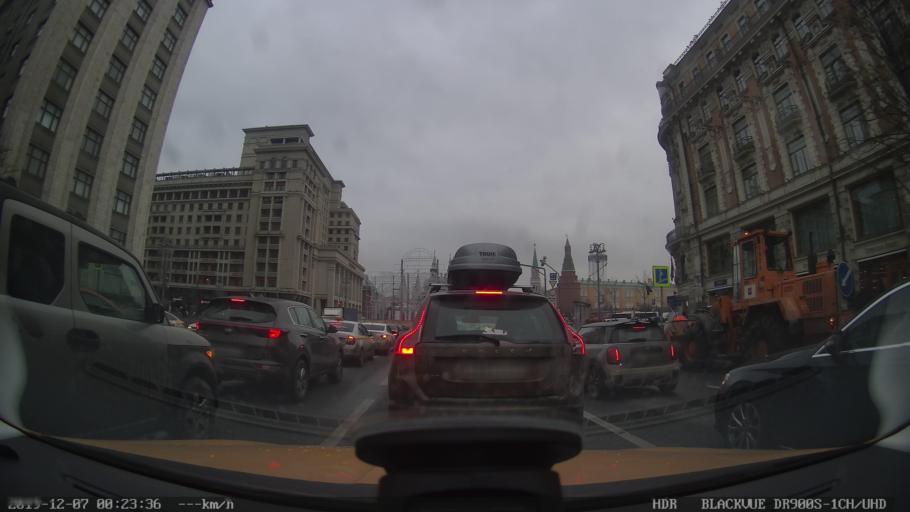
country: RU
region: Moscow
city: Zapadnoye Degunino
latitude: 55.8504
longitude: 37.5274
